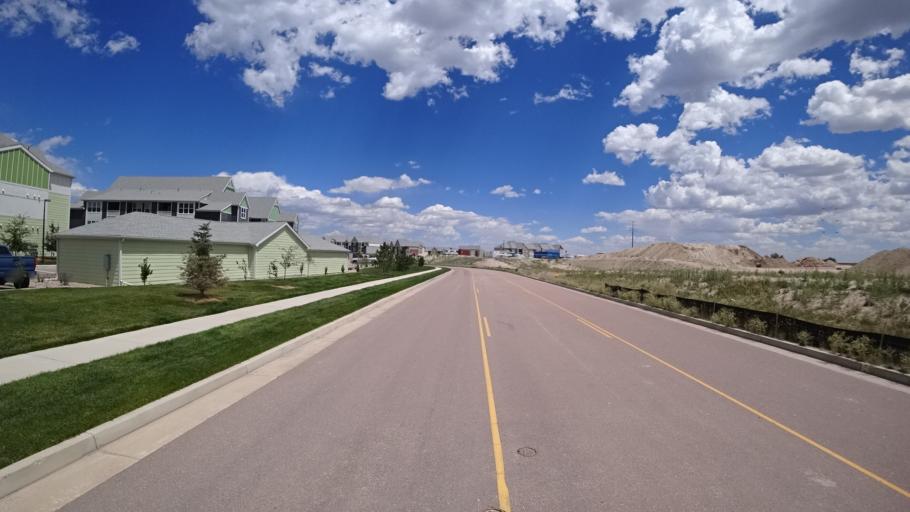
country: US
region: Colorado
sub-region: El Paso County
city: Black Forest
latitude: 38.9425
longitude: -104.7100
